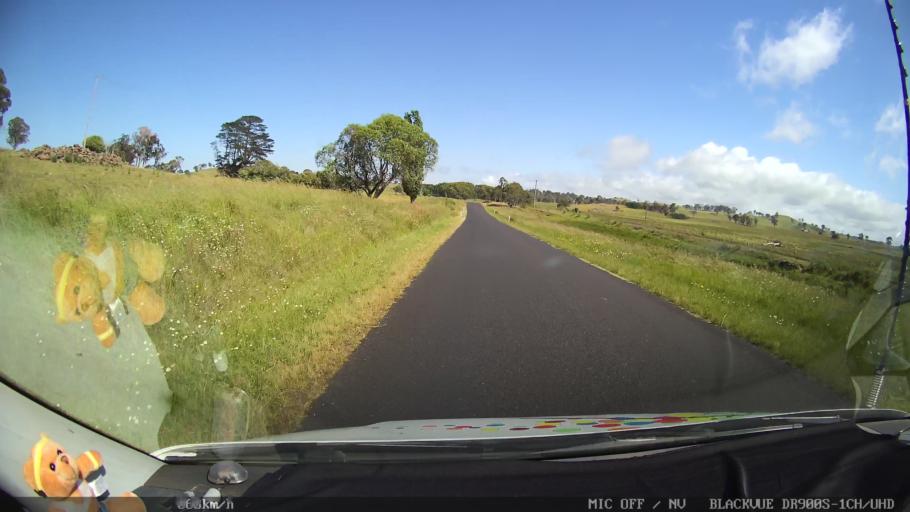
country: AU
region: New South Wales
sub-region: Guyra
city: Guyra
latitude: -30.0778
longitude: 151.6762
